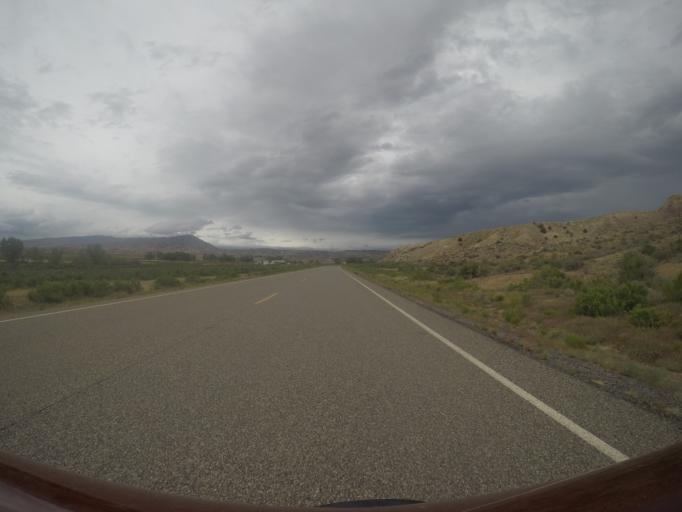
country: US
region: Wyoming
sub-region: Big Horn County
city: Lovell
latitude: 44.9560
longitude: -108.2924
